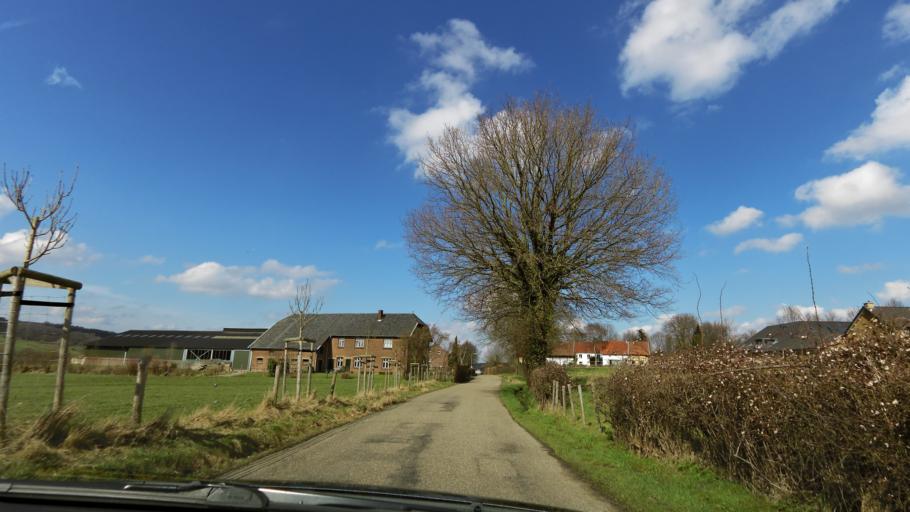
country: BE
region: Wallonia
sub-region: Province de Liege
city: Plombieres
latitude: 50.7884
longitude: 5.9289
